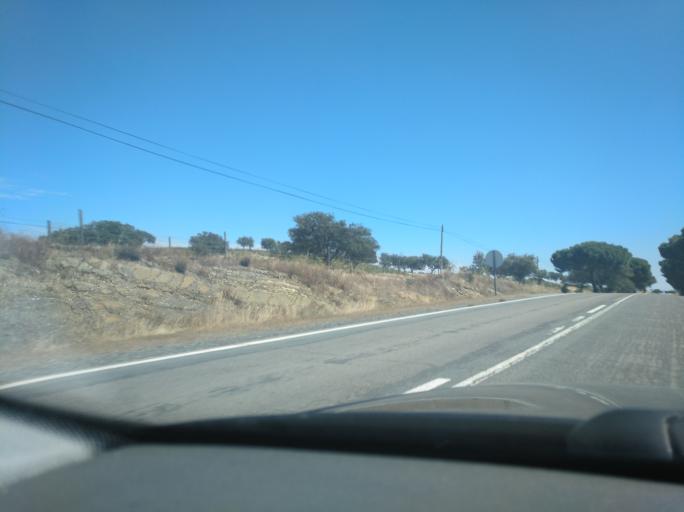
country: PT
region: Beja
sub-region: Almodovar
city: Almodovar
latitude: 37.5830
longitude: -8.0780
